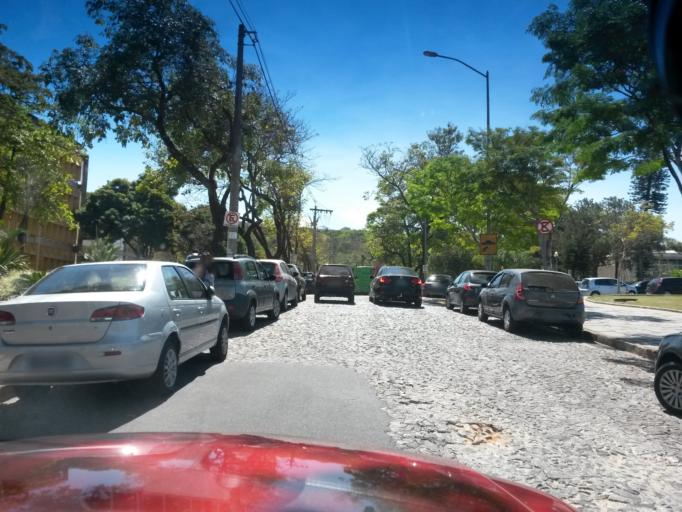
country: BR
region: Minas Gerais
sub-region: Belo Horizonte
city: Belo Horizonte
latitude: -19.8672
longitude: -43.9646
